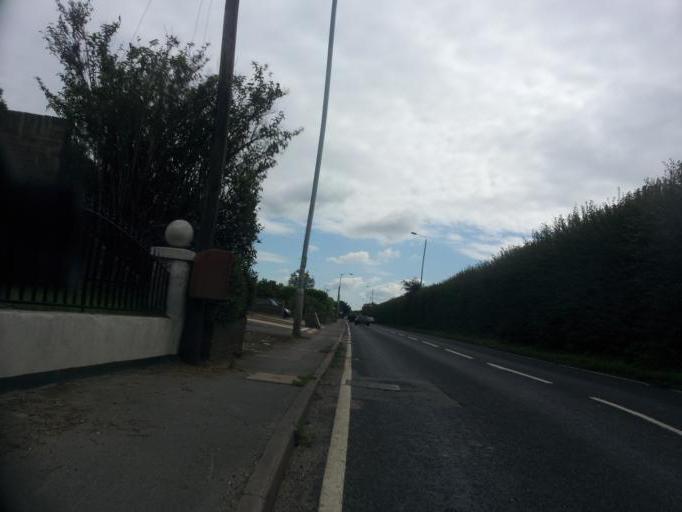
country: GB
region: England
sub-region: Kent
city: Newington
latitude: 51.3537
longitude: 0.6583
